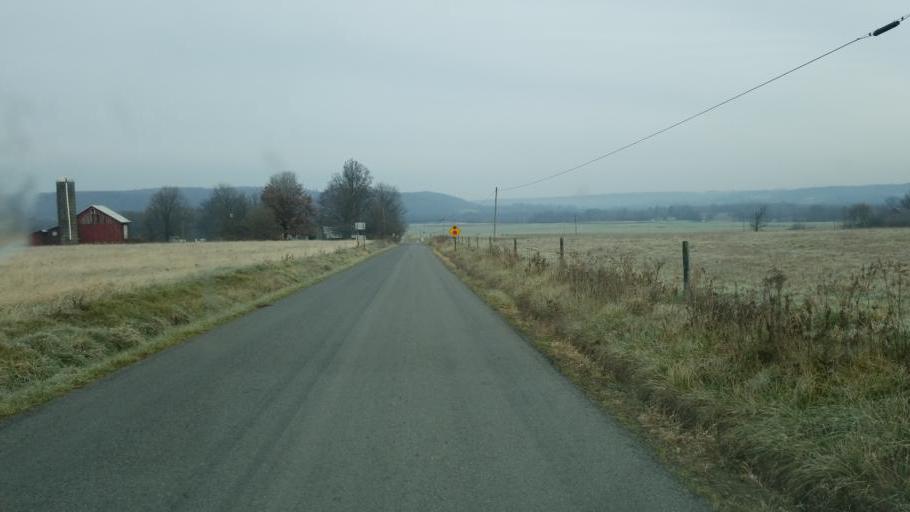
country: US
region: Pennsylvania
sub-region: Crawford County
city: Cochranton
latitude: 41.5243
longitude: -80.1247
